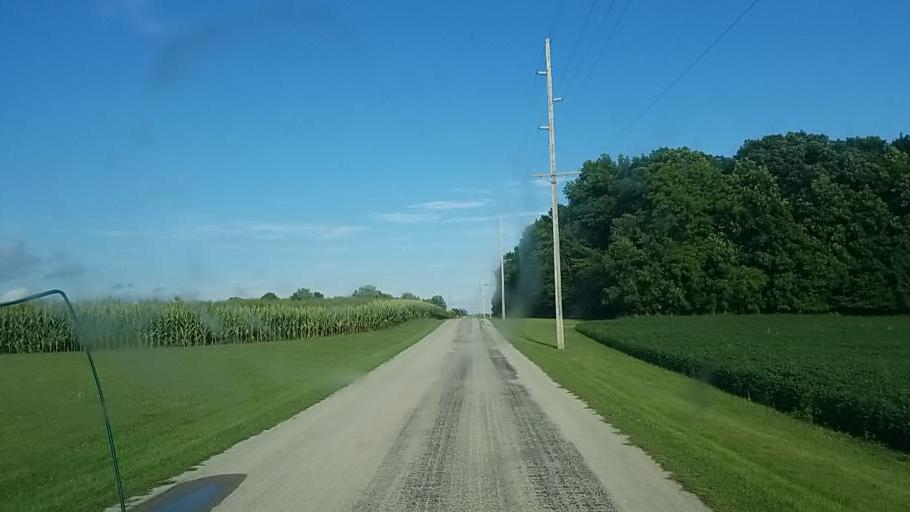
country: US
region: Ohio
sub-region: Wyandot County
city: Upper Sandusky
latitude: 40.8146
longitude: -83.1715
